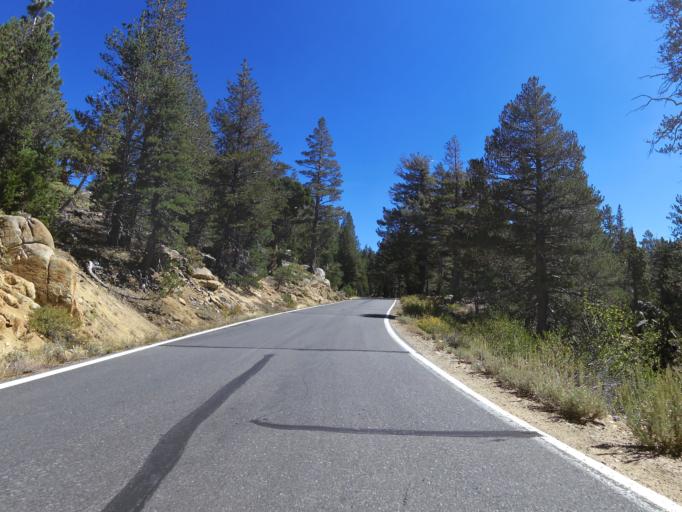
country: US
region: Nevada
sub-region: Douglas County
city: Gardnerville Ranchos
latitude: 38.5435
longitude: -119.8179
